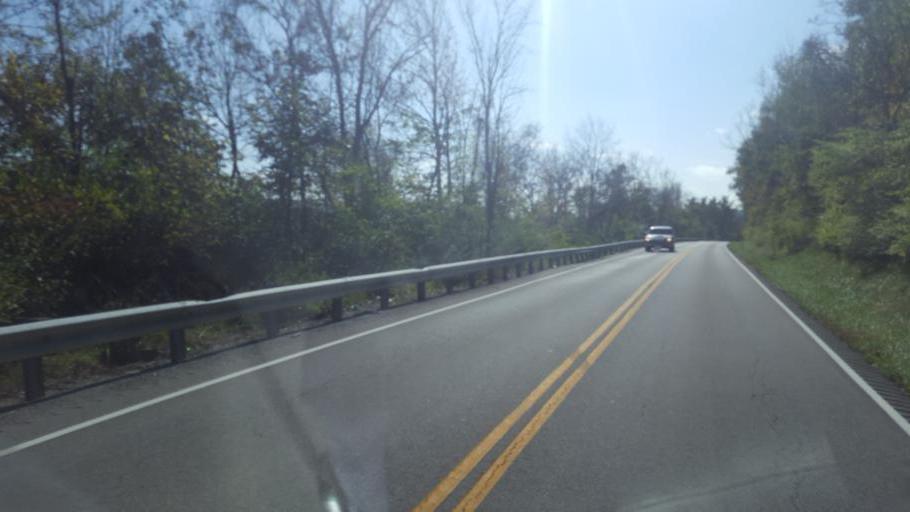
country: US
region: Ohio
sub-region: Brown County
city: Aberdeen
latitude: 38.6794
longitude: -83.7841
